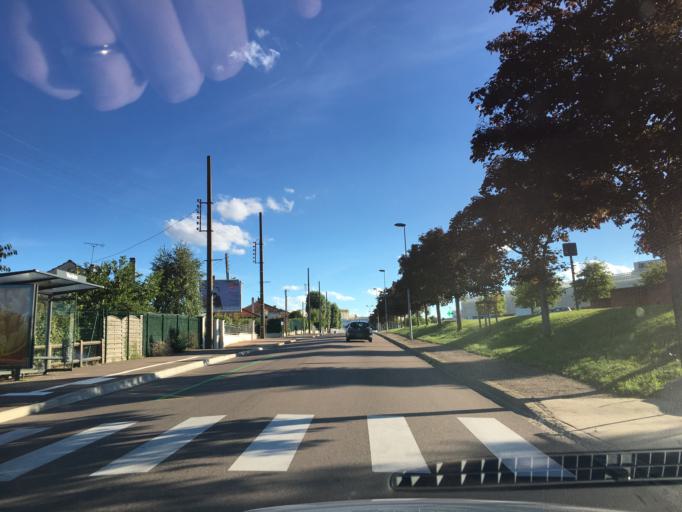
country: FR
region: Bourgogne
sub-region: Departement de l'Yonne
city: Auxerre
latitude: 47.8081
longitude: 3.5583
